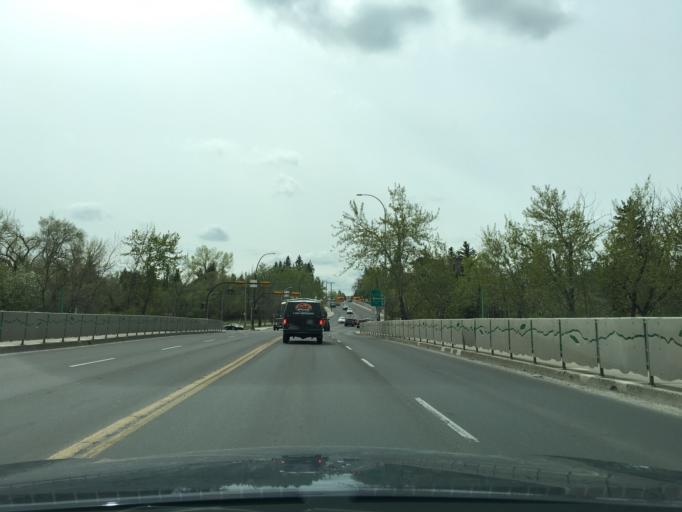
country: CA
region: Alberta
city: Calgary
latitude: 51.0180
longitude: -114.0779
